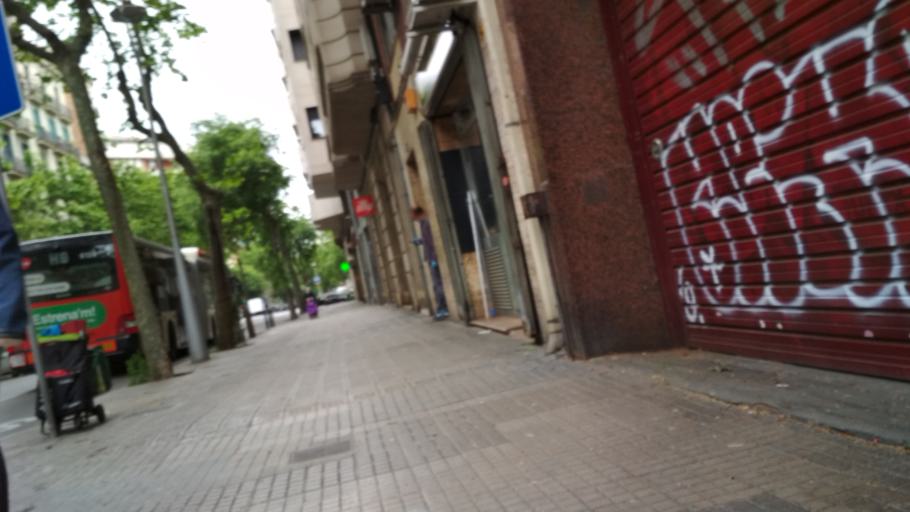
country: ES
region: Catalonia
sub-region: Provincia de Barcelona
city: Gracia
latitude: 41.4052
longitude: 2.1689
